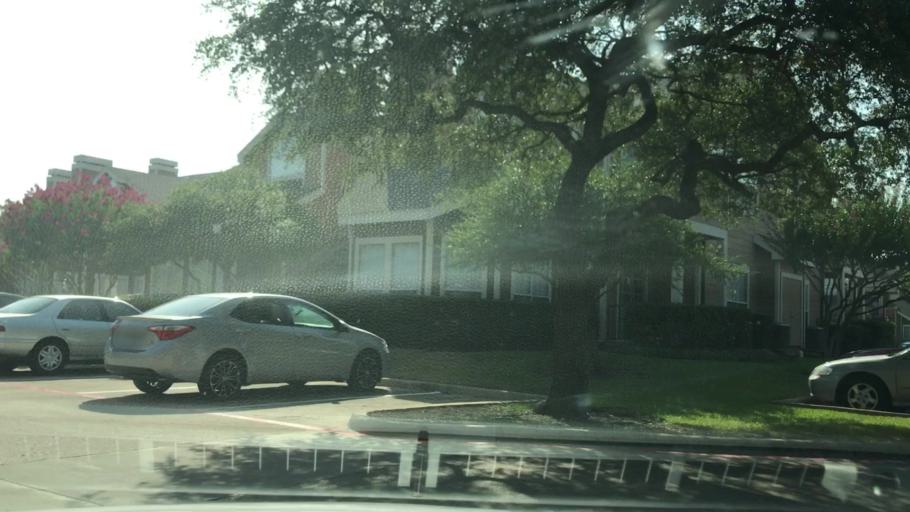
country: US
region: Texas
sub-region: Dallas County
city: Farmers Branch
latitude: 32.9379
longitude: -96.9447
